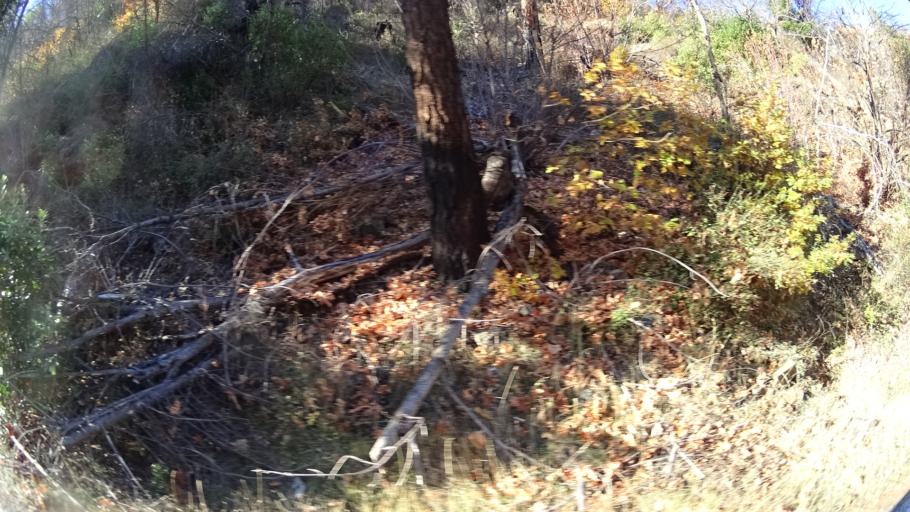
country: US
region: California
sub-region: Siskiyou County
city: Yreka
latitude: 41.9090
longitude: -122.8361
